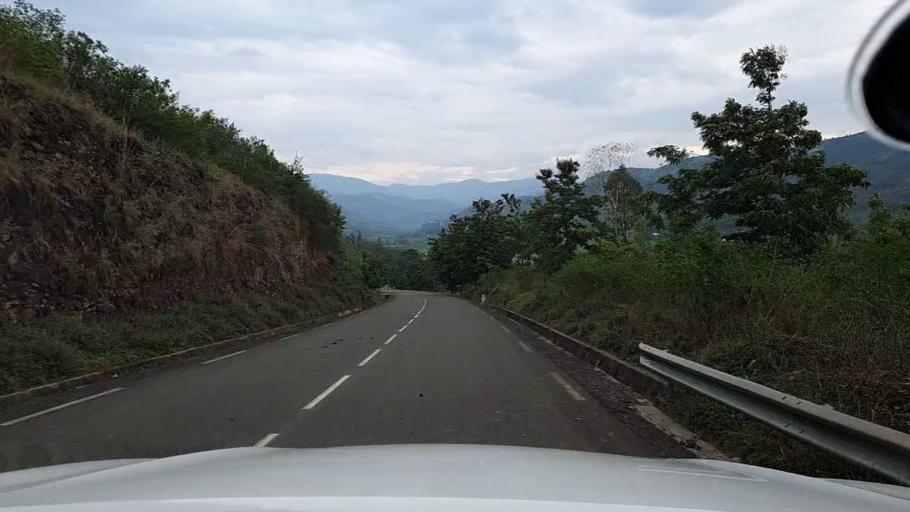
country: BI
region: Cibitoke
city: Cibitoke
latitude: -2.7343
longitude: 29.0381
